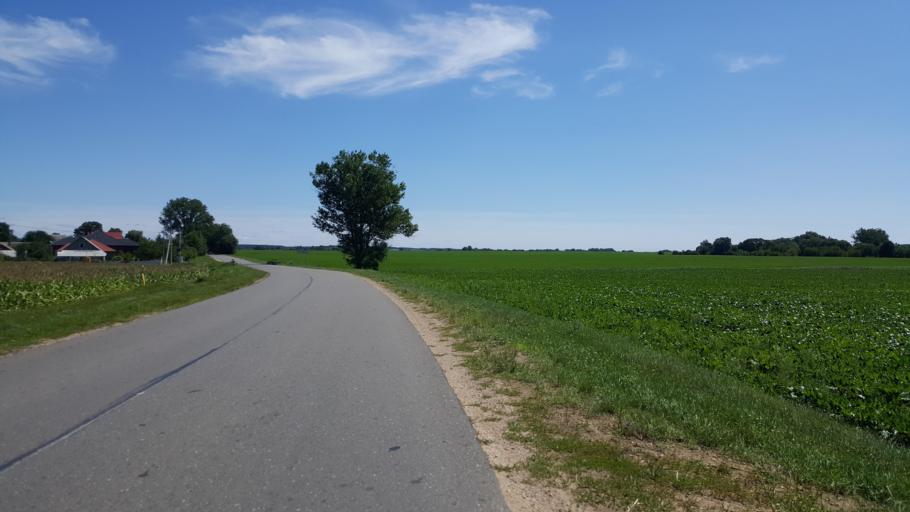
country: BY
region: Brest
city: Charnawchytsy
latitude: 52.2199
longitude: 23.7536
